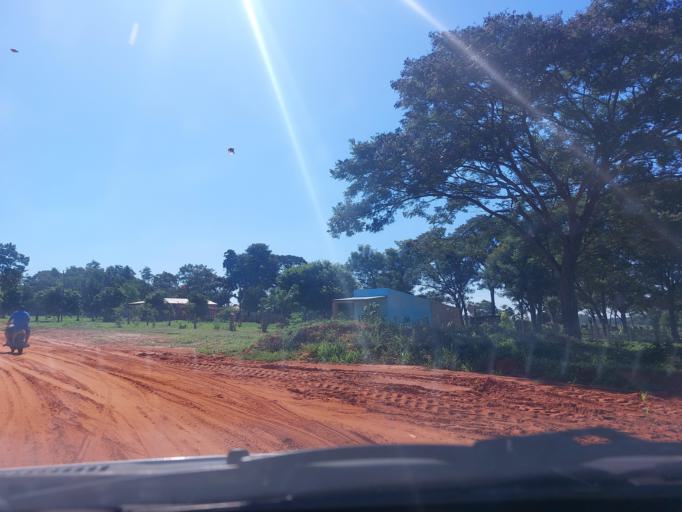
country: PY
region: San Pedro
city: Lima
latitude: -24.1622
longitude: -56.0115
